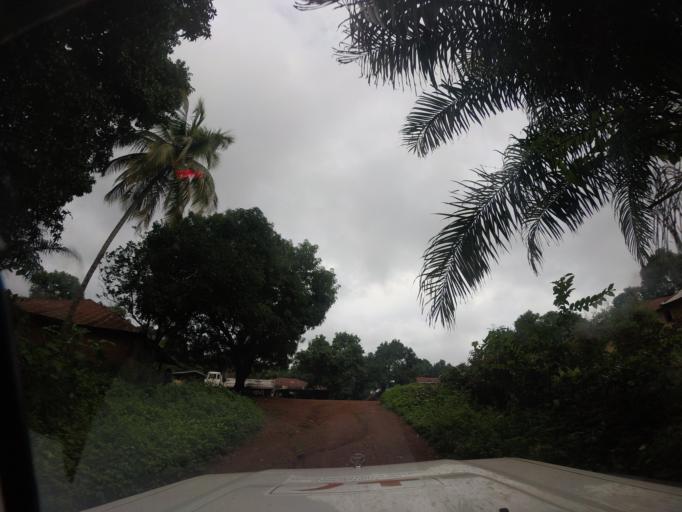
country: SL
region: Northern Province
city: Kamakwie
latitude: 9.6763
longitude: -12.2246
